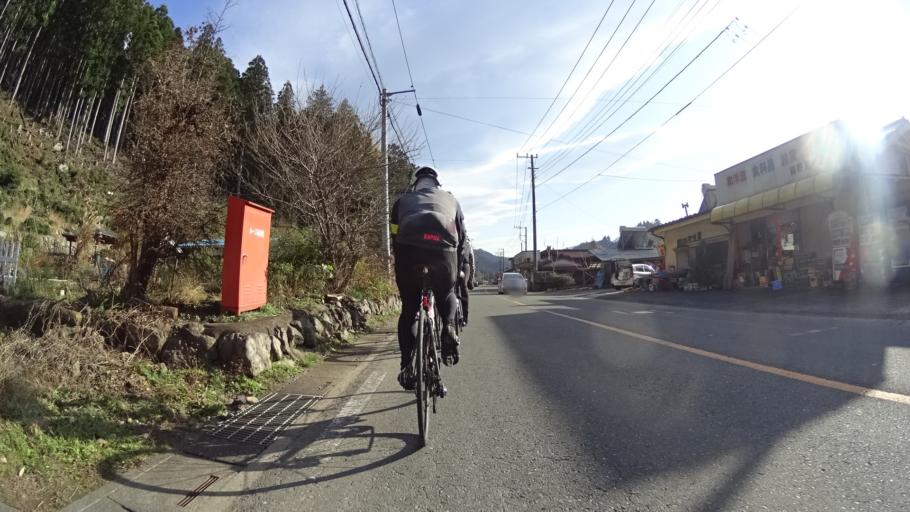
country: JP
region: Tokyo
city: Ome
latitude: 35.8837
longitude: 139.1834
